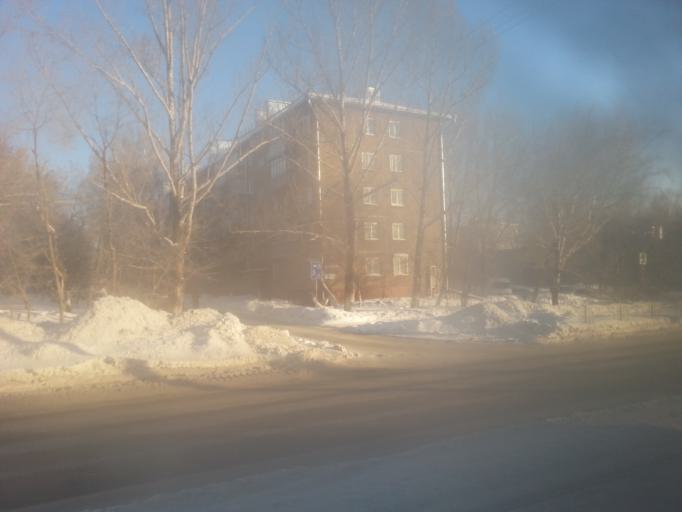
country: RU
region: Altai Krai
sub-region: Gorod Barnaulskiy
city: Barnaul
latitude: 53.3575
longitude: 83.7085
